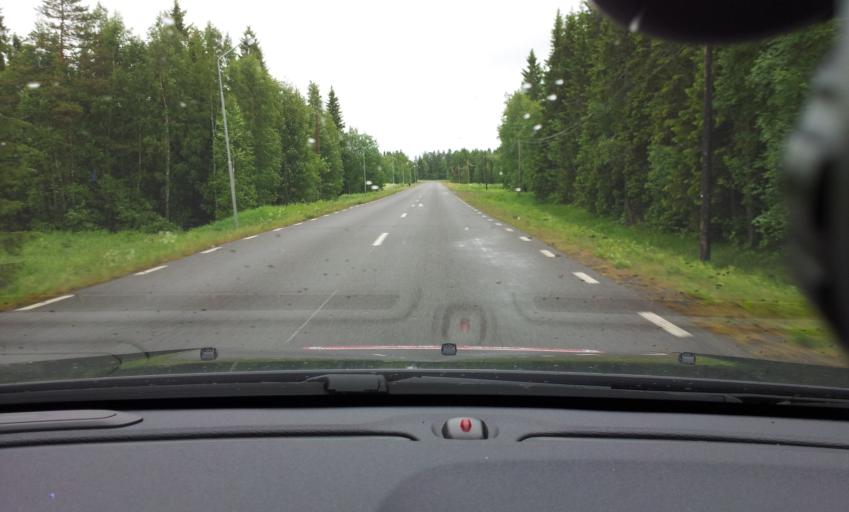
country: SE
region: Jaemtland
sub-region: OEstersunds Kommun
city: Lit
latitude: 63.6723
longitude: 15.0775
